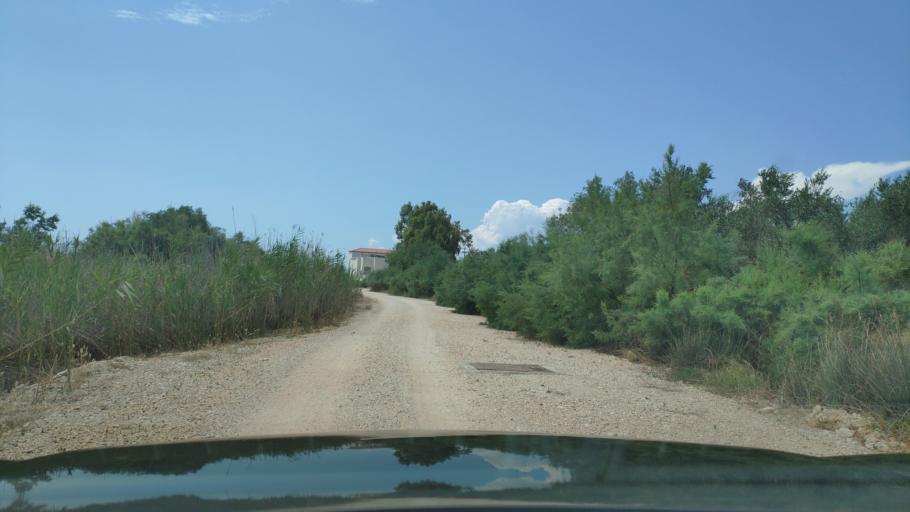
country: GR
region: West Greece
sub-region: Nomos Aitolias kai Akarnanias
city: Menidi
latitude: 39.0516
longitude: 21.1030
